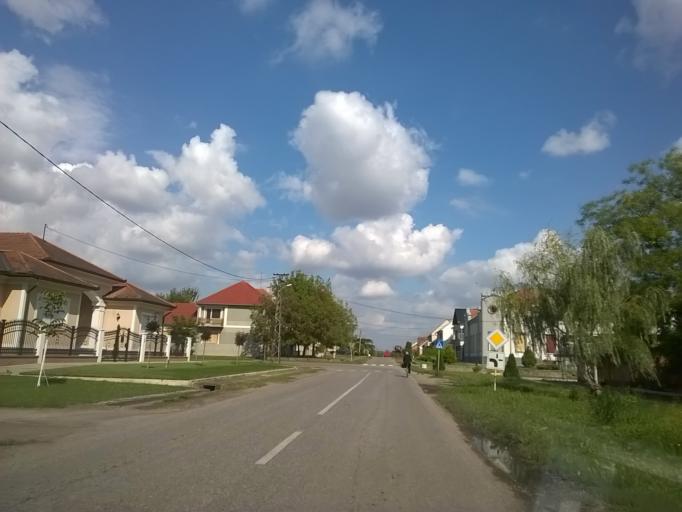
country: RS
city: Lokve
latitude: 45.1531
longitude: 21.0314
